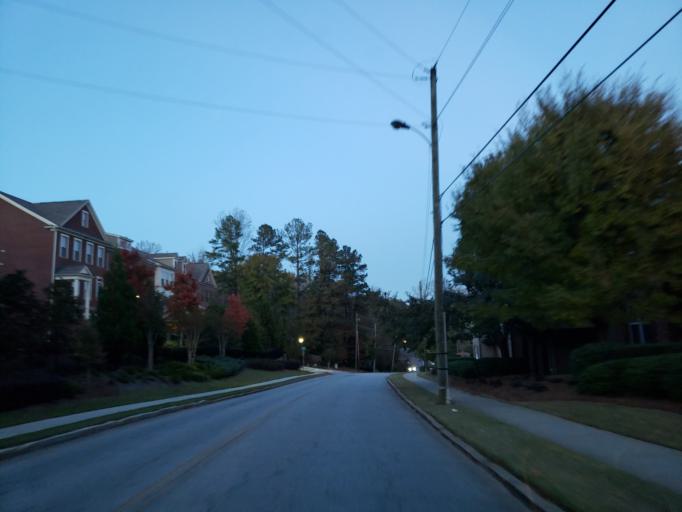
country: US
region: Georgia
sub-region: DeKalb County
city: Chamblee
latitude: 33.8955
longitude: -84.3246
